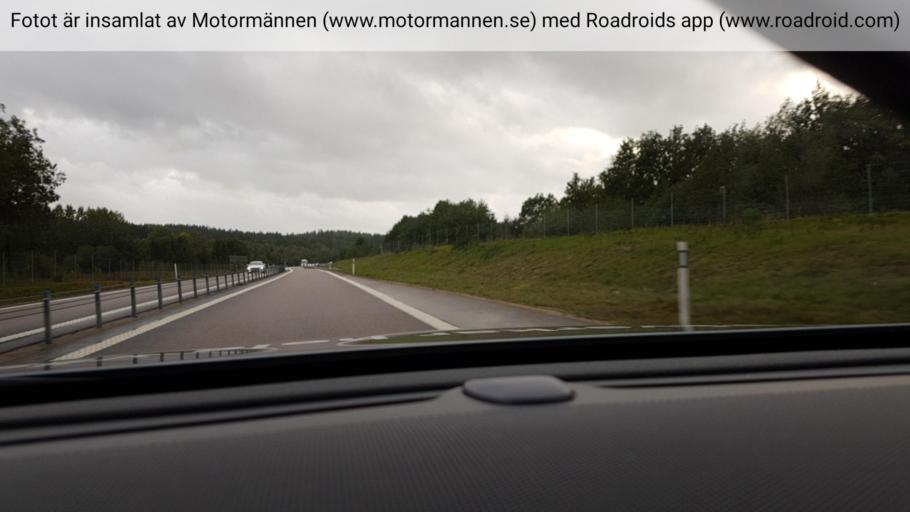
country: SE
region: Vaestra Goetaland
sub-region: Uddevalla Kommun
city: Uddevalla
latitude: 58.3327
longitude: 11.9767
